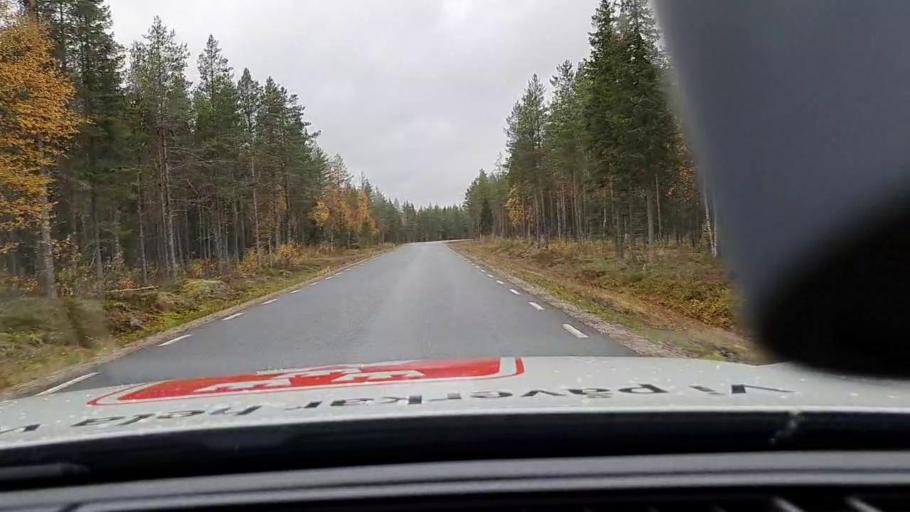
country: SE
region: Norrbotten
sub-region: Haparanda Kommun
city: Haparanda
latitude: 65.9380
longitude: 23.8063
